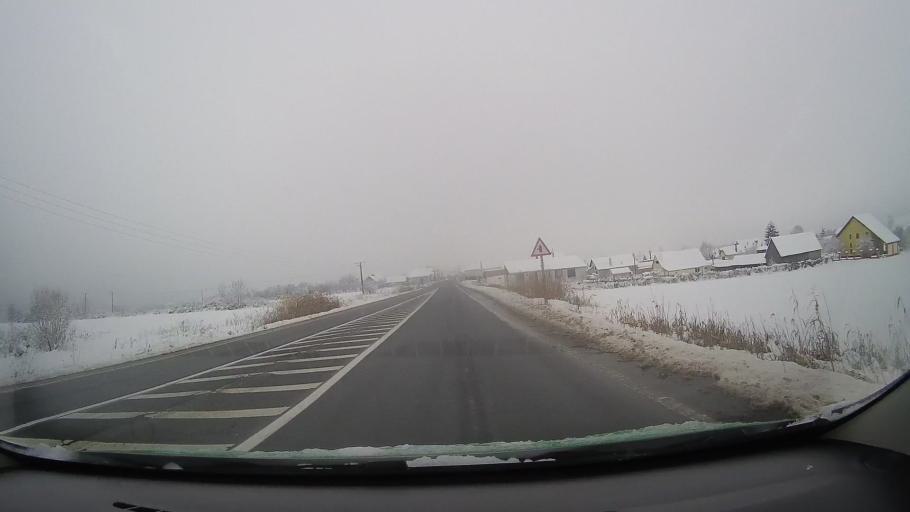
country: RO
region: Sibiu
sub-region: Oras Saliste
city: Saliste
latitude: 45.7866
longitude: 23.9326
